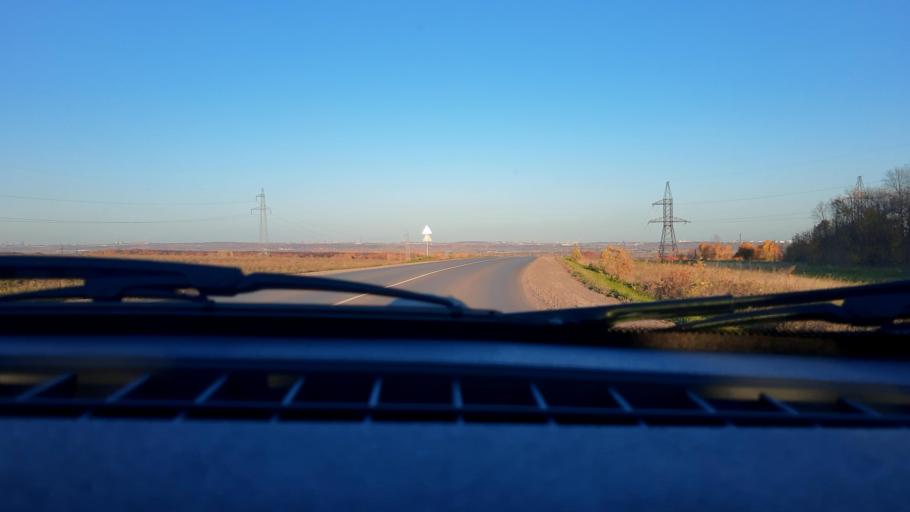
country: RU
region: Bashkortostan
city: Mikhaylovka
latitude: 54.8299
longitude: 55.8866
